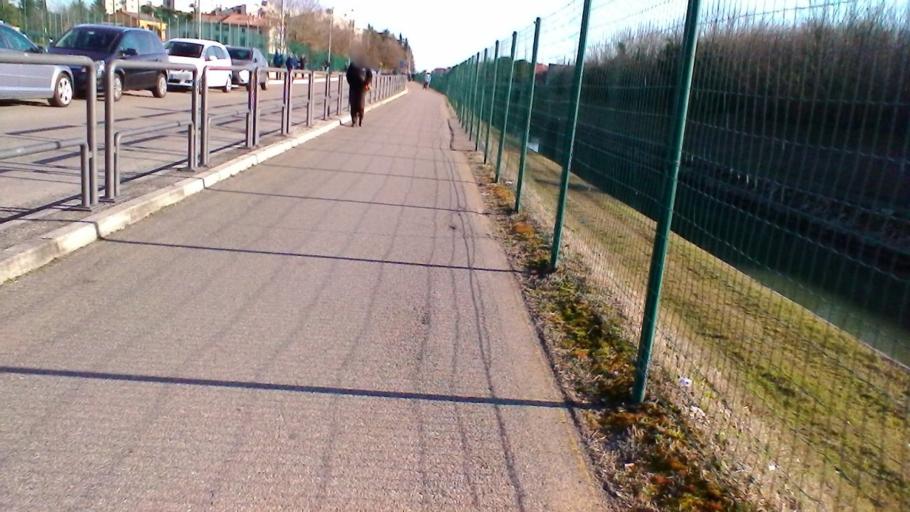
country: IT
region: Veneto
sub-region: Provincia di Verona
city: Parona
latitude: 45.4549
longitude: 10.9590
